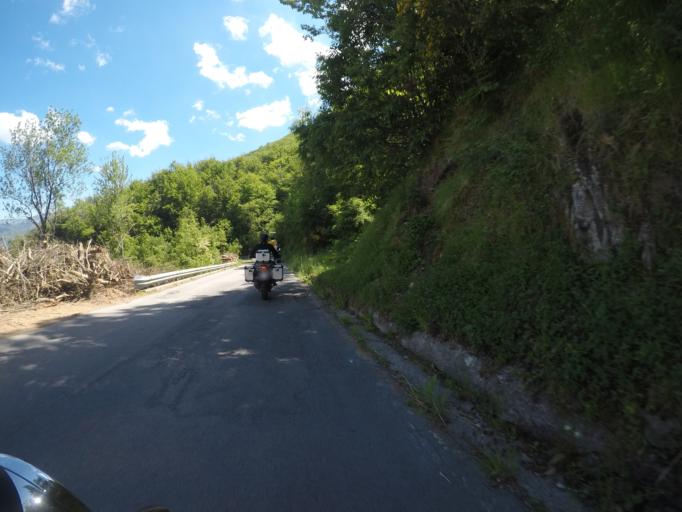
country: IT
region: Tuscany
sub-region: Provincia di Lucca
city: Careggine
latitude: 44.1258
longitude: 10.3342
